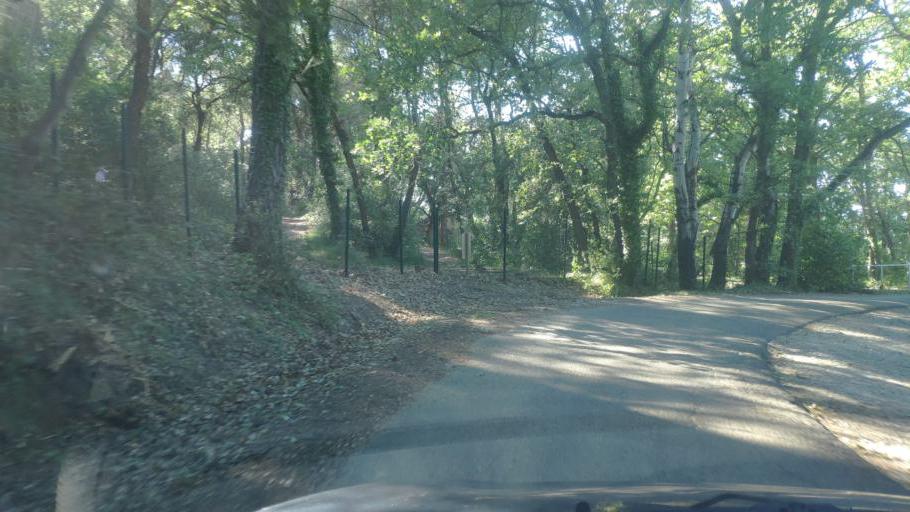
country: FR
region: Provence-Alpes-Cote d'Azur
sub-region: Departement du Vaucluse
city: Aubignan
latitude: 44.0847
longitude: 5.0410
